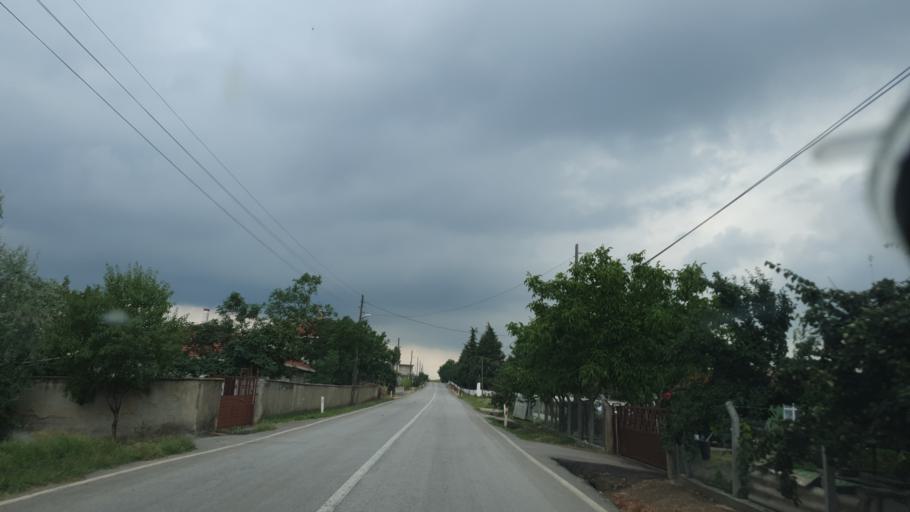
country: TR
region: Tekirdag
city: Hayrabolu
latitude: 41.2192
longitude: 26.9797
